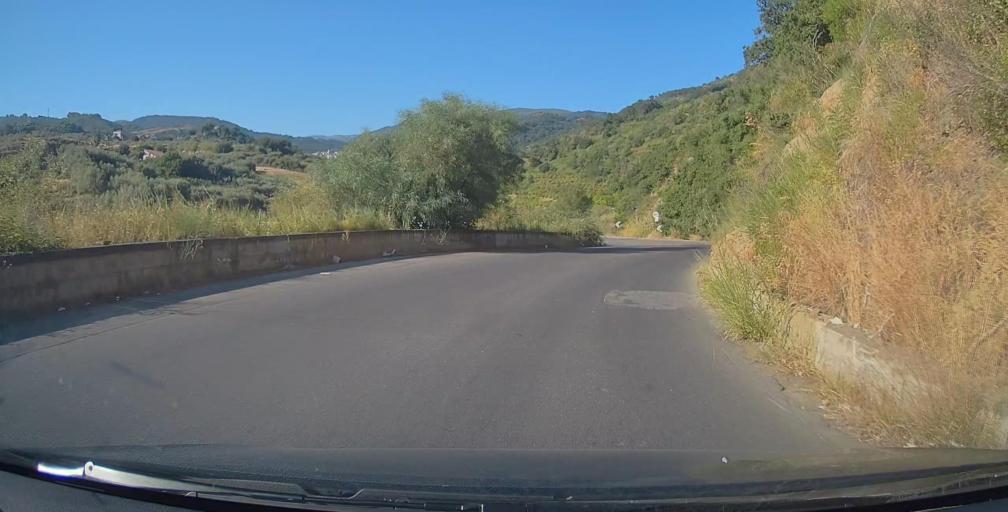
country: IT
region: Sicily
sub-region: Messina
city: Librizzi
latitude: 38.0778
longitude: 14.9721
